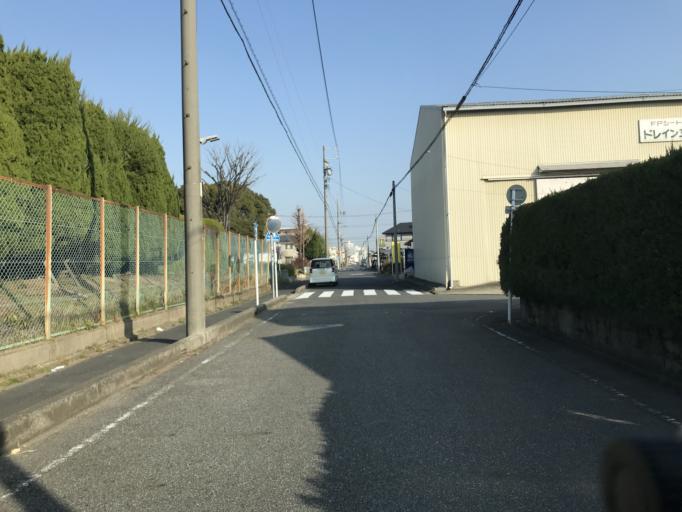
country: JP
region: Aichi
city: Nagoya-shi
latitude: 35.2085
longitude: 136.8686
